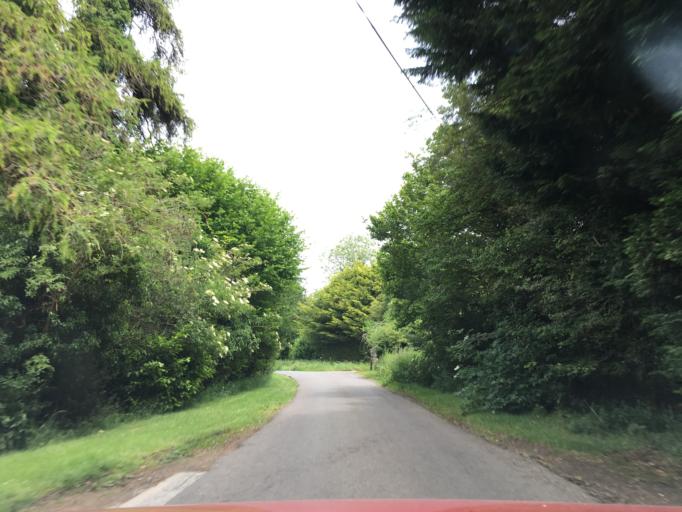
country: GB
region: England
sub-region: Wiltshire
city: Royal Wootton Bassett
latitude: 51.5630
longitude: -1.9063
